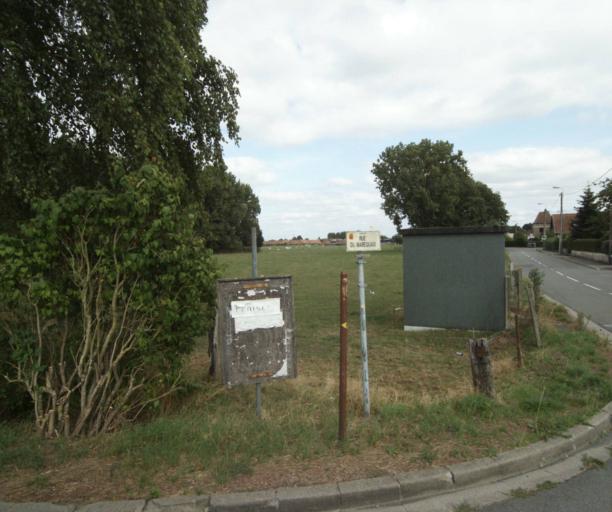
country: FR
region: Nord-Pas-de-Calais
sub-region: Departement du Nord
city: Chereng
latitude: 50.6161
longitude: 3.2189
